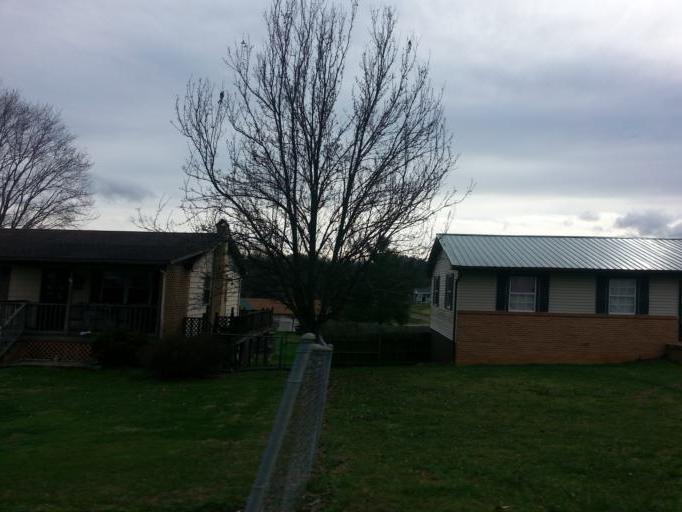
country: US
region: Tennessee
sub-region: Greene County
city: Greeneville
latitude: 36.1269
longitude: -82.8927
